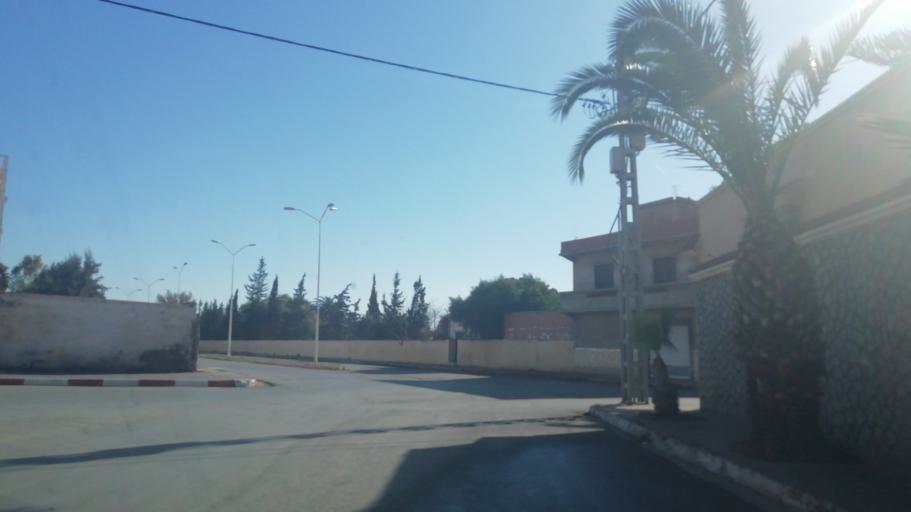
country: DZ
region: Oran
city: Oran
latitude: 35.6750
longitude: -0.6338
